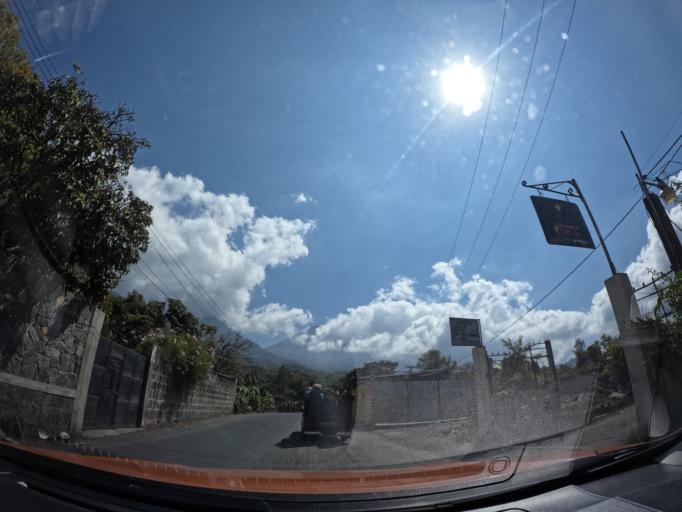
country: GT
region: Solola
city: Santiago Atitlan
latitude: 14.6298
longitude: -91.2318
